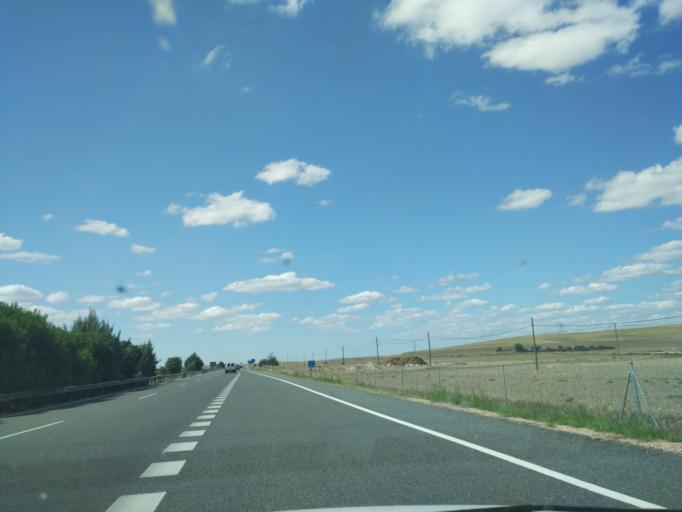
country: ES
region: Castille and Leon
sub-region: Provincia de Valladolid
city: Ataquines
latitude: 41.1840
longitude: -4.8088
